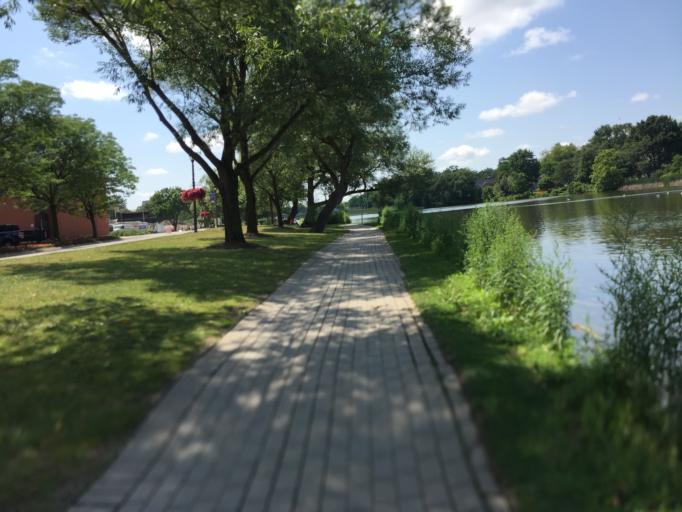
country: CA
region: Ontario
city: Stratford
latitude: 43.3748
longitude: -80.9758
